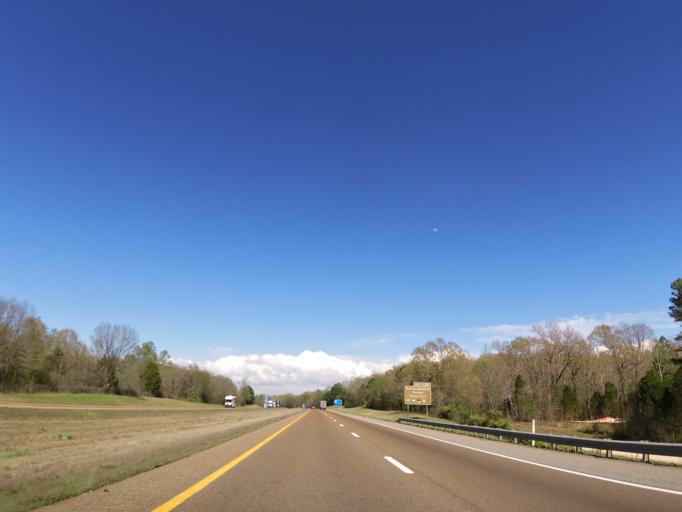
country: US
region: Tennessee
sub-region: Decatur County
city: Parsons
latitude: 35.8273
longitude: -88.1130
